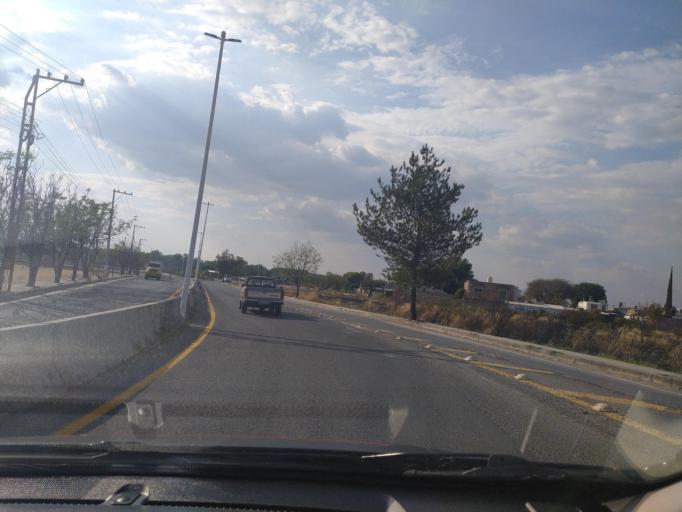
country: MX
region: Guanajuato
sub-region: San Francisco del Rincon
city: Estacion de San Francisco
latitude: 21.0348
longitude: -101.8245
